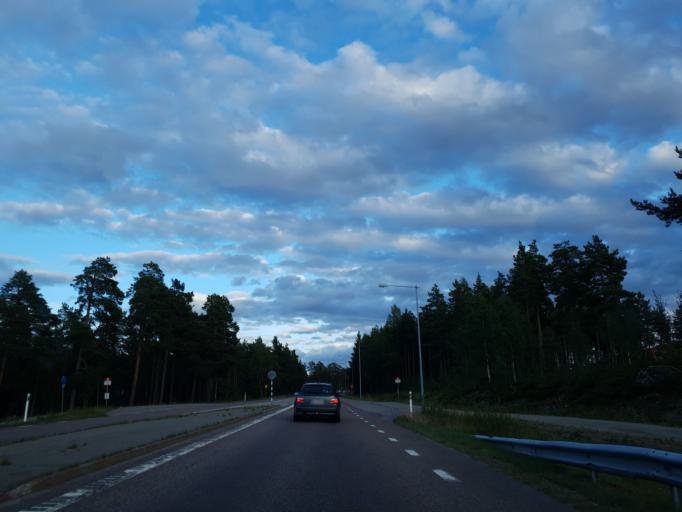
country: SE
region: Gaevleborg
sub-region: Soderhamns Kommun
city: Soderhamn
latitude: 61.2917
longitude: 17.0722
